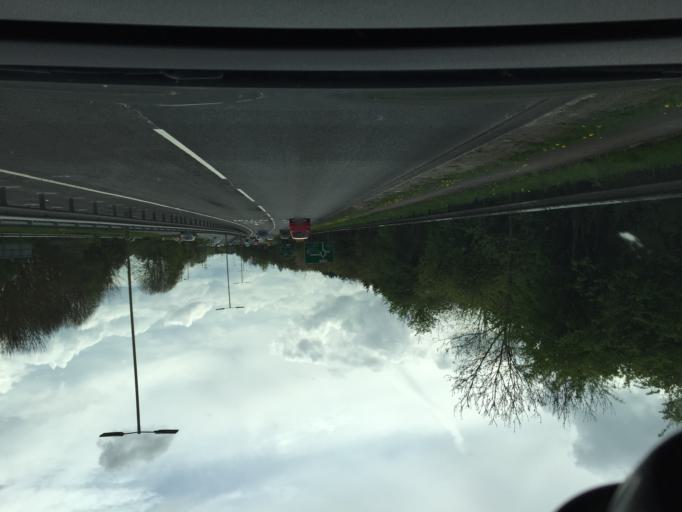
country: GB
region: England
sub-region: Oxfordshire
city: Oxford
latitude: 51.7278
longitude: -1.2535
